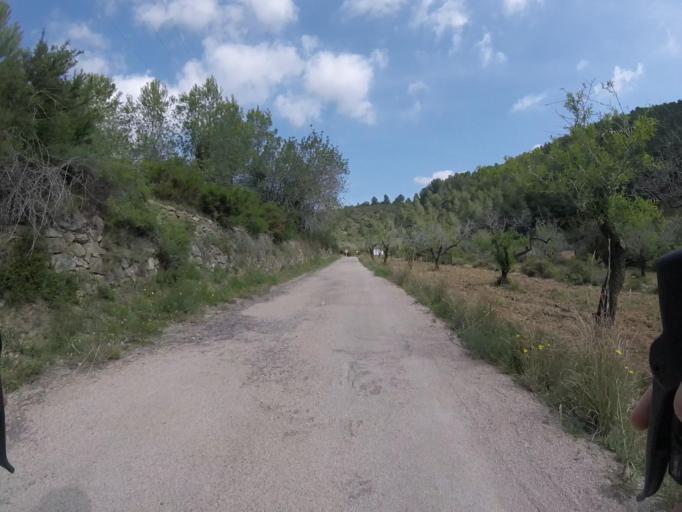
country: ES
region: Valencia
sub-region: Provincia de Castello
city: Cabanes
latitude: 40.1157
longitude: 0.0476
